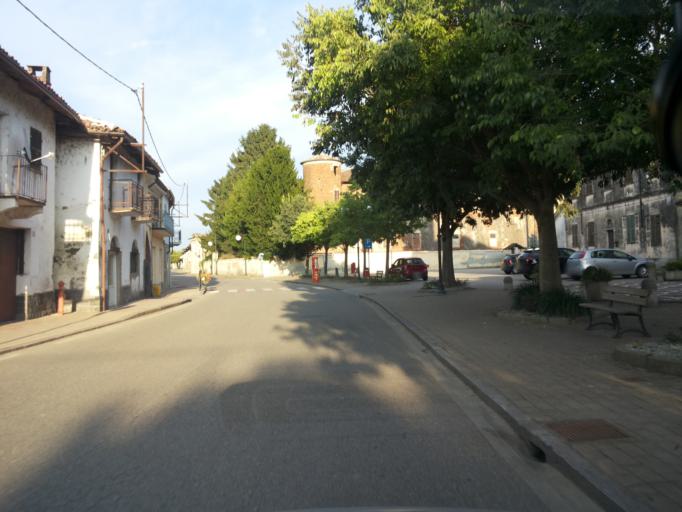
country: IT
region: Piedmont
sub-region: Provincia di Vercelli
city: Salasco
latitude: 45.3254
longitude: 8.2641
